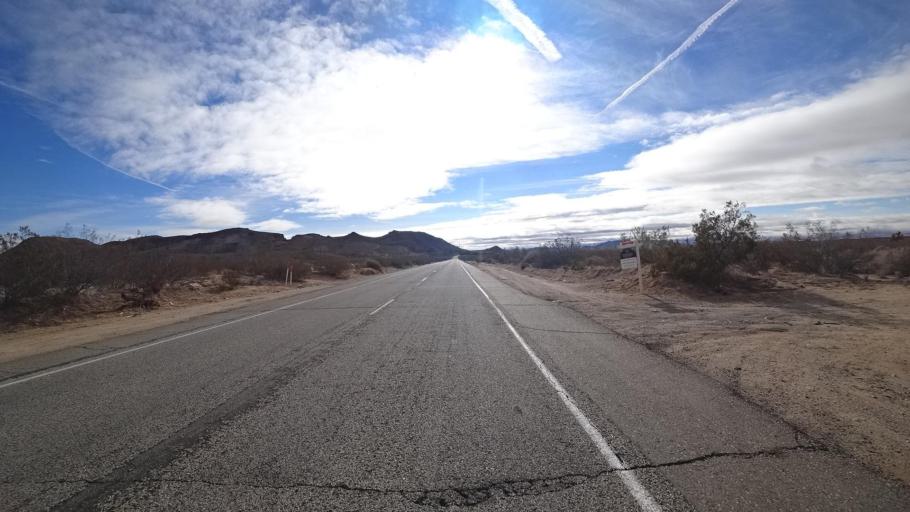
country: US
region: California
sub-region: Kern County
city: Mojave
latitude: 34.9657
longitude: -118.2992
